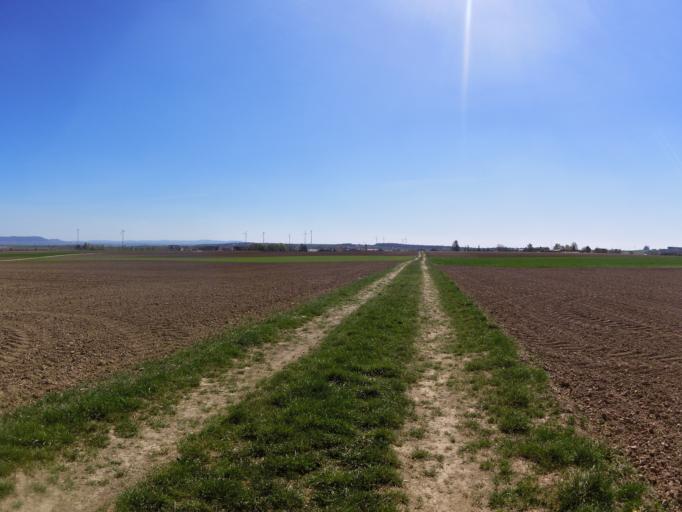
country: DE
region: Bavaria
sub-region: Regierungsbezirk Unterfranken
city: Biebelried
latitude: 49.8037
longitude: 10.0830
